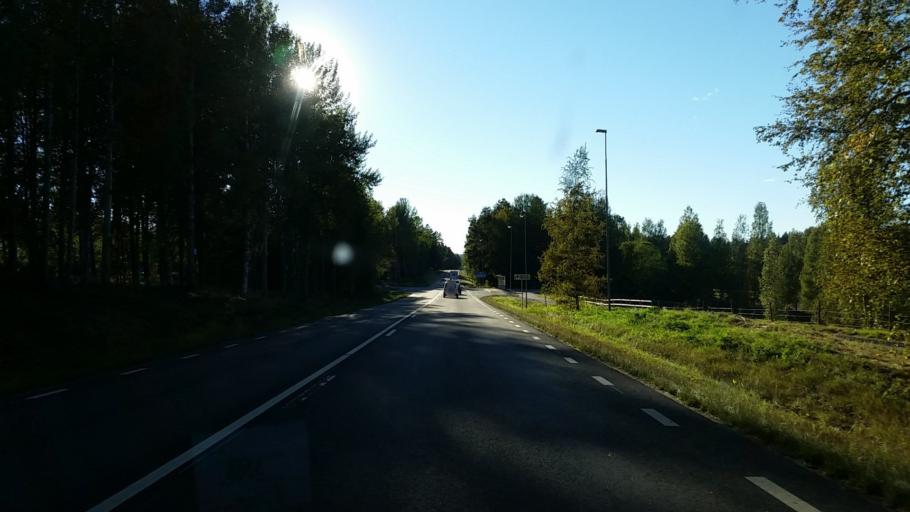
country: SE
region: Gaevleborg
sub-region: Hudiksvalls Kommun
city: Delsbo
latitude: 61.7986
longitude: 16.5412
